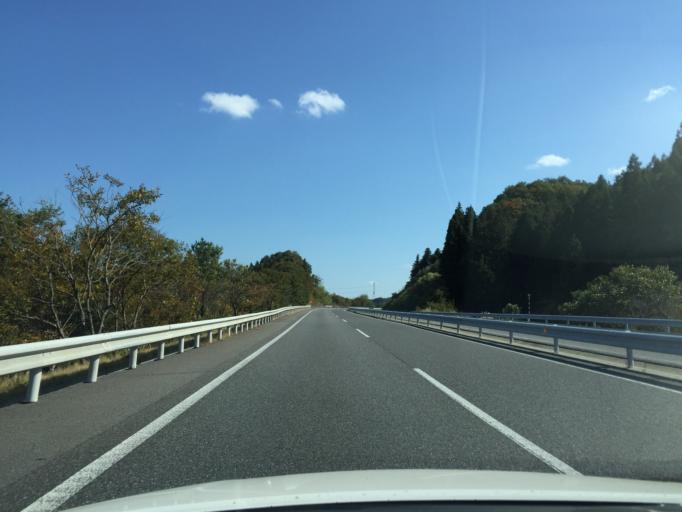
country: JP
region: Fukushima
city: Funehikimachi-funehiki
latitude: 37.2538
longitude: 140.6544
